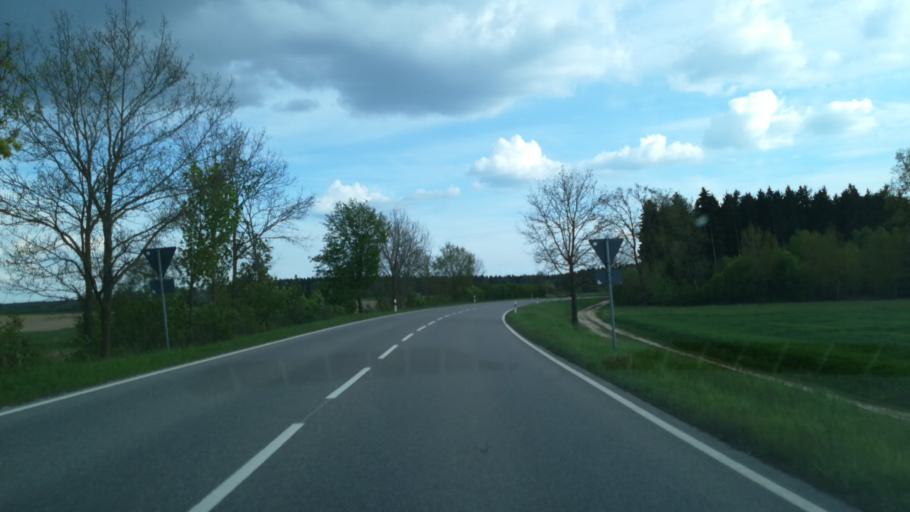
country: DE
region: Baden-Wuerttemberg
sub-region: Tuebingen Region
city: Messkirch
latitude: 47.9891
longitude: 9.0787
